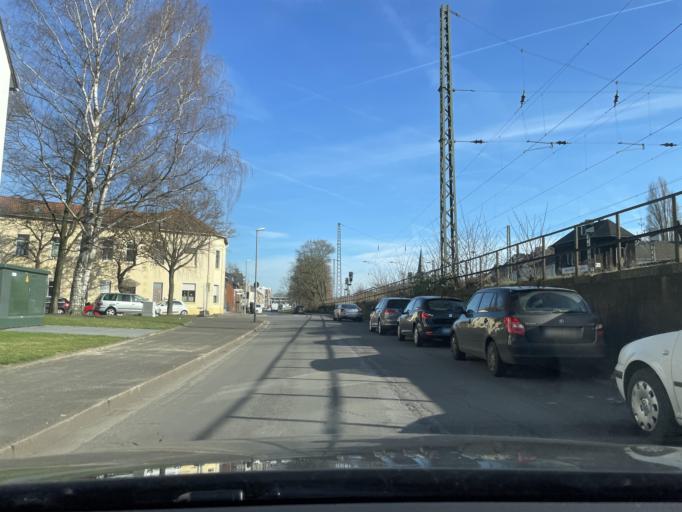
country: DE
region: North Rhine-Westphalia
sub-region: Regierungsbezirk Dusseldorf
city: Krefeld
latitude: 51.3298
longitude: 6.6062
